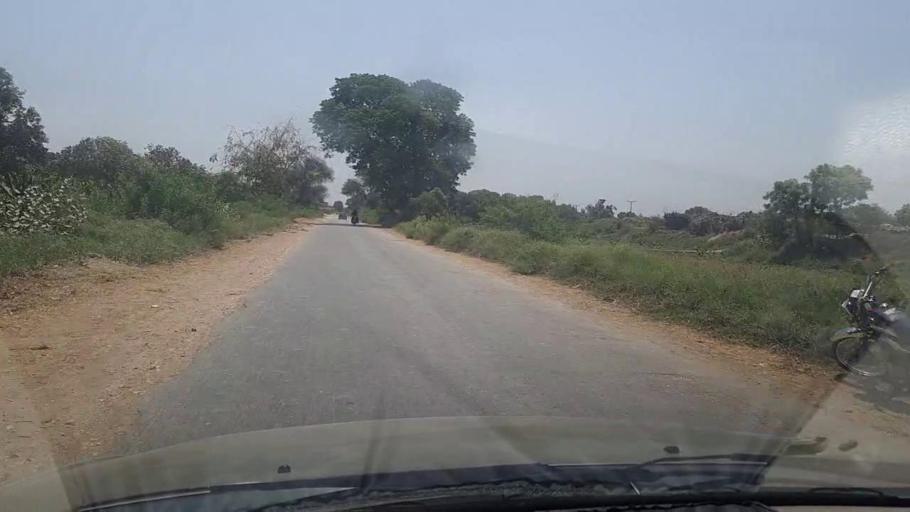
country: PK
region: Sindh
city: Tando Jam
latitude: 25.3024
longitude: 68.5821
